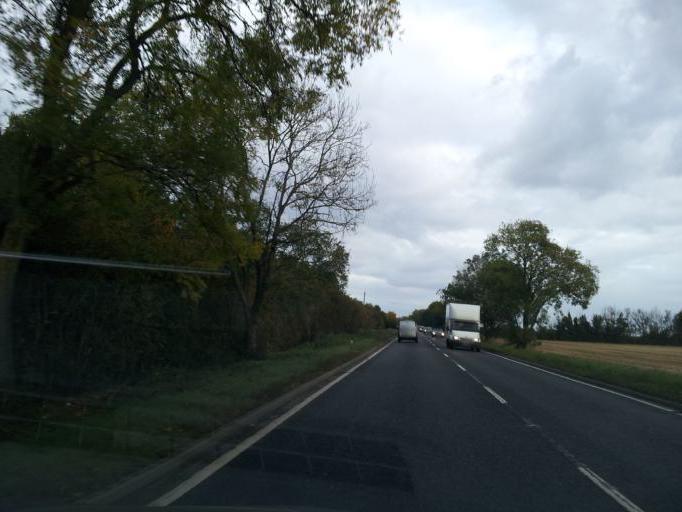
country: GB
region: England
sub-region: Cambridgeshire
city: Papworth Everard
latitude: 52.2279
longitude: -0.1180
